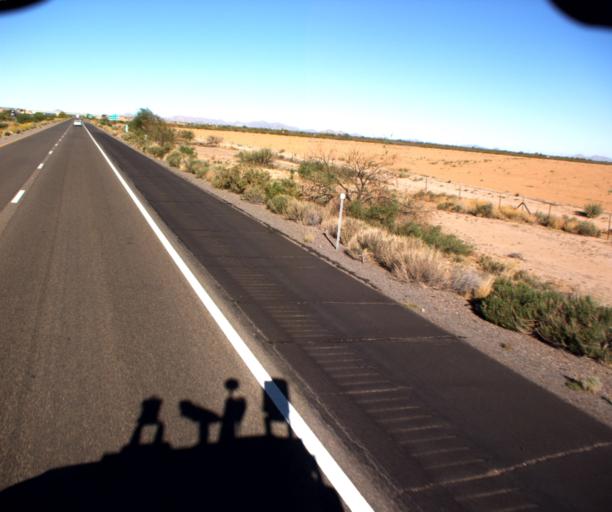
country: US
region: Arizona
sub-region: Pinal County
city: Casa Grande
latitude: 32.8284
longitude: -111.9544
